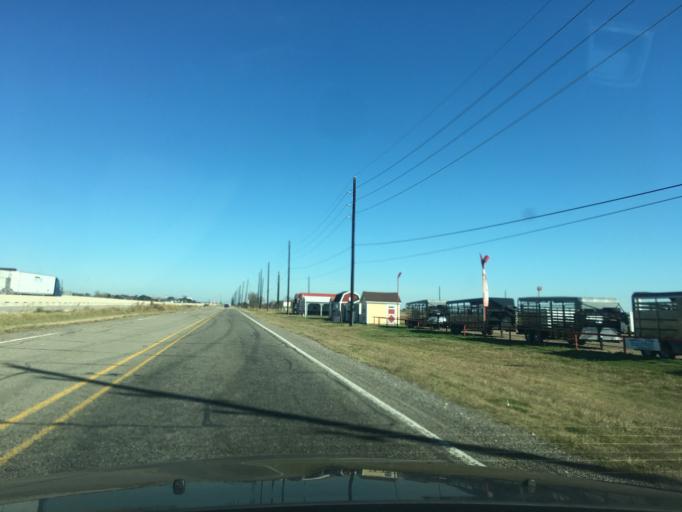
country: US
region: Texas
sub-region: Fort Bend County
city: Pleak
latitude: 29.4864
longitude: -95.9306
